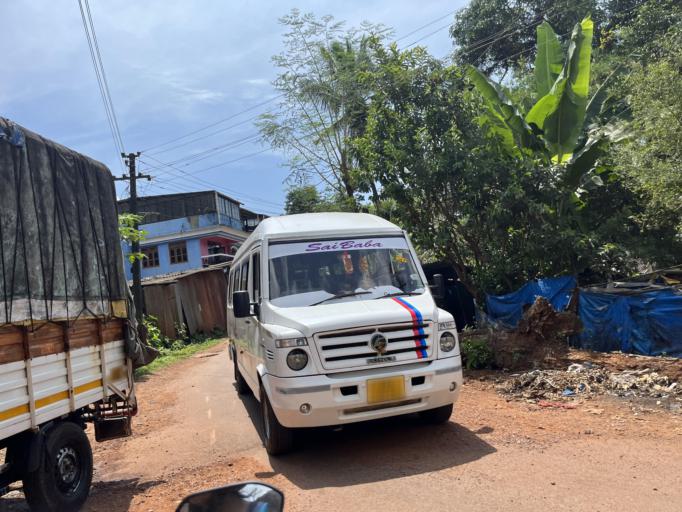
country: IN
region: Goa
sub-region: North Goa
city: Ponda
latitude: 15.4070
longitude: 74.0120
